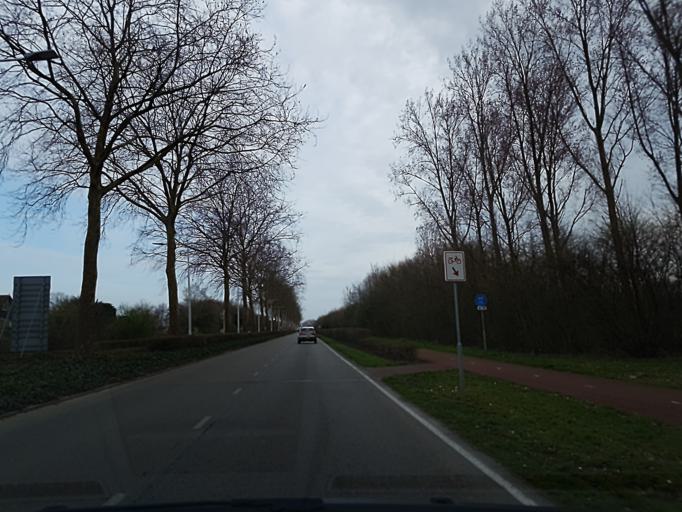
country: NL
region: Zeeland
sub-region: Gemeente Terneuzen
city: Terneuzen
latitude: 51.3125
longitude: 3.8495
